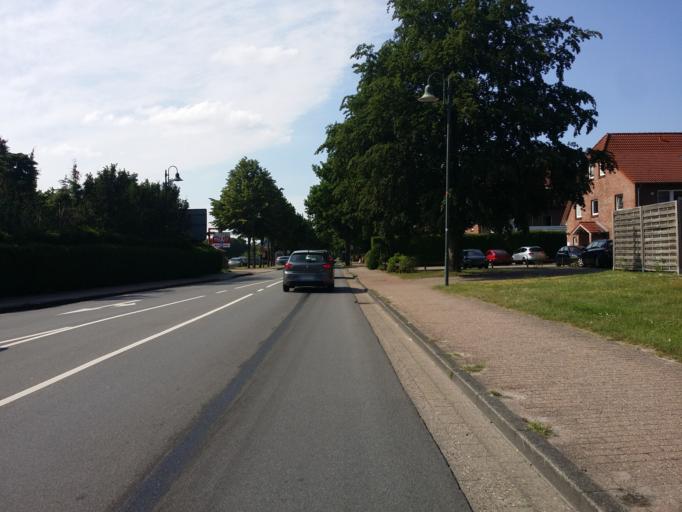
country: DE
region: Lower Saxony
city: Wiefelstede
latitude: 53.2602
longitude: 8.1148
